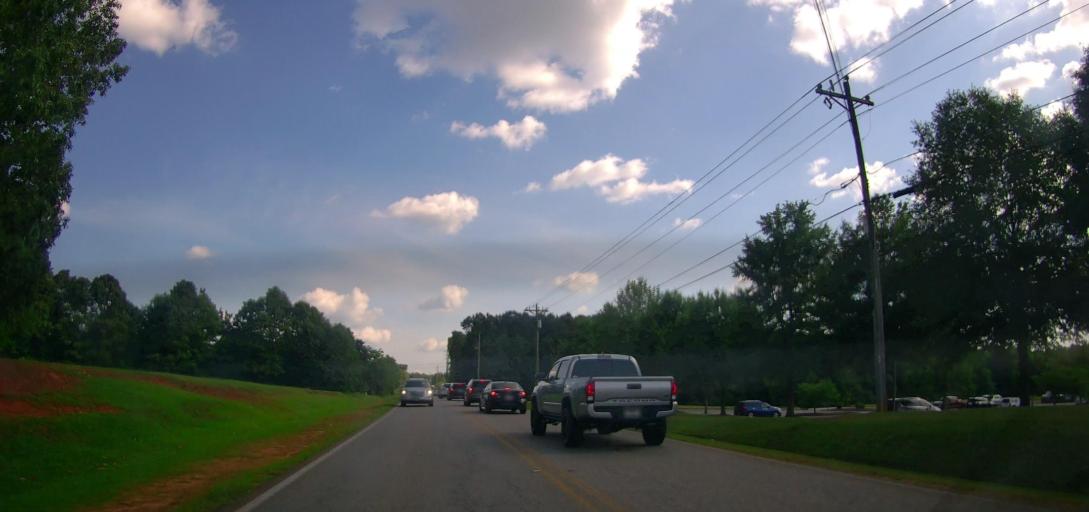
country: US
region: Georgia
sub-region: Henry County
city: McDonough
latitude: 33.4371
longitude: -84.2068
